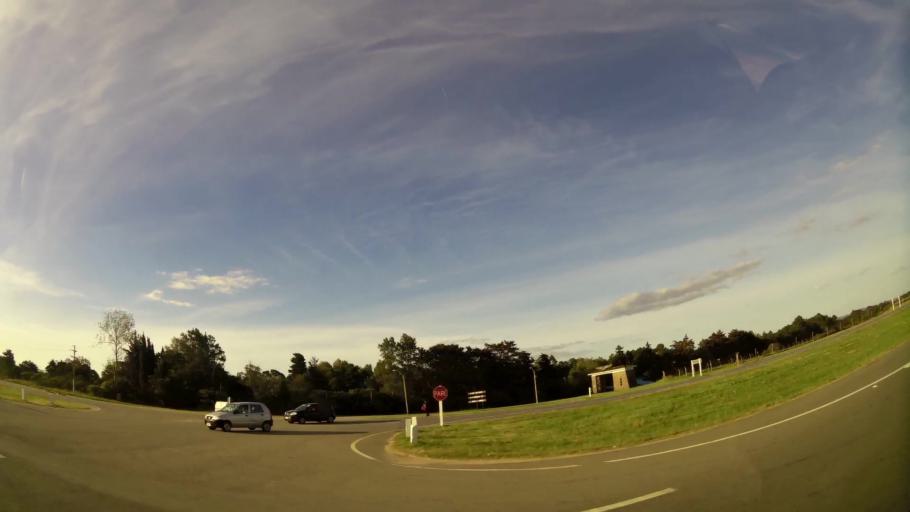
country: UY
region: Maldonado
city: Pan de Azucar
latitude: -34.8634
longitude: -55.1242
